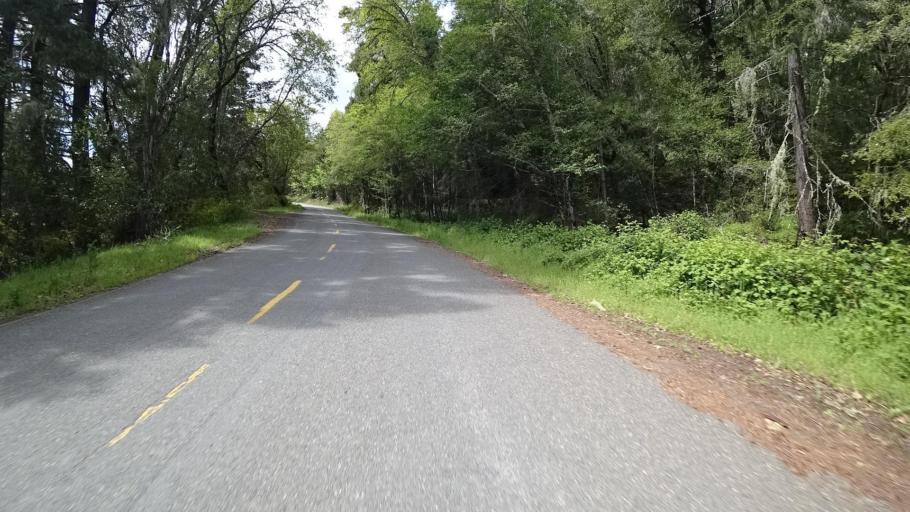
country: US
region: California
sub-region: Humboldt County
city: Redway
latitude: 40.1507
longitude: -123.6260
